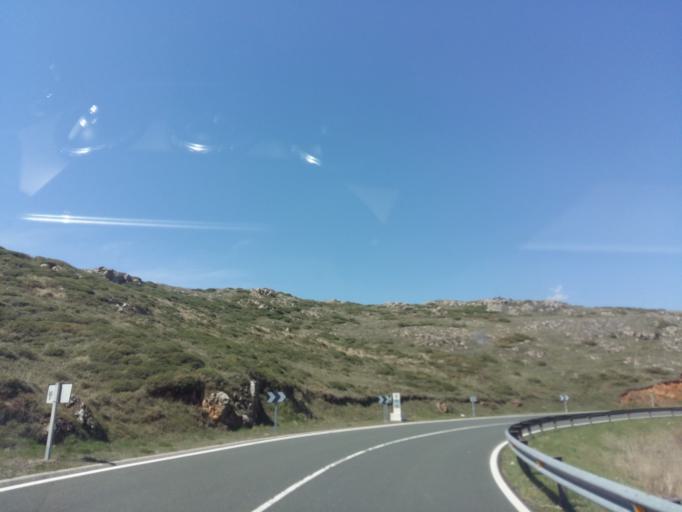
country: ES
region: Cantabria
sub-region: Provincia de Cantabria
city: Mataporquera
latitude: 42.8831
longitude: -4.1693
